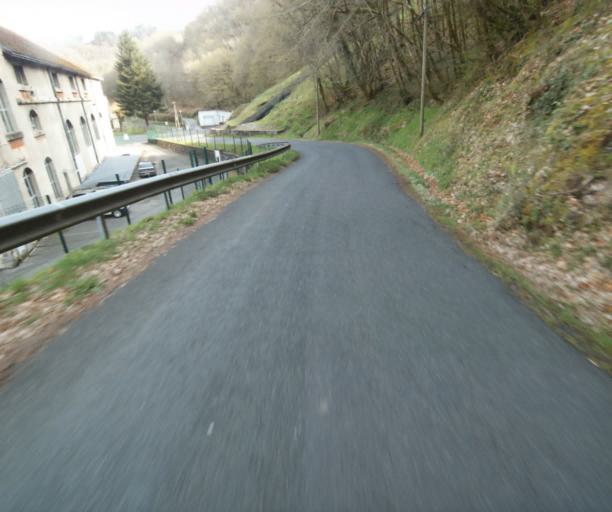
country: FR
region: Limousin
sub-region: Departement de la Correze
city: Correze
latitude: 45.3438
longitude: 1.8240
